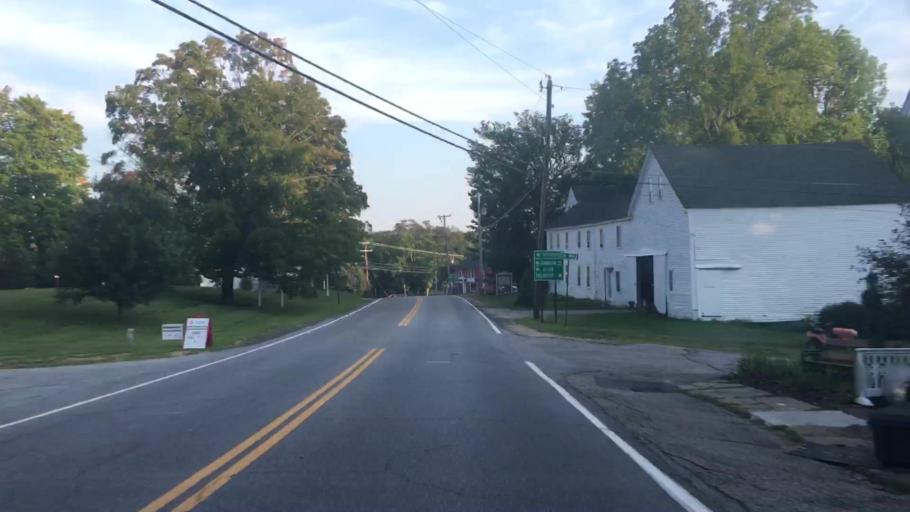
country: US
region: New Hampshire
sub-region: Belknap County
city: Gilmanton
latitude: 43.4253
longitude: -71.4144
